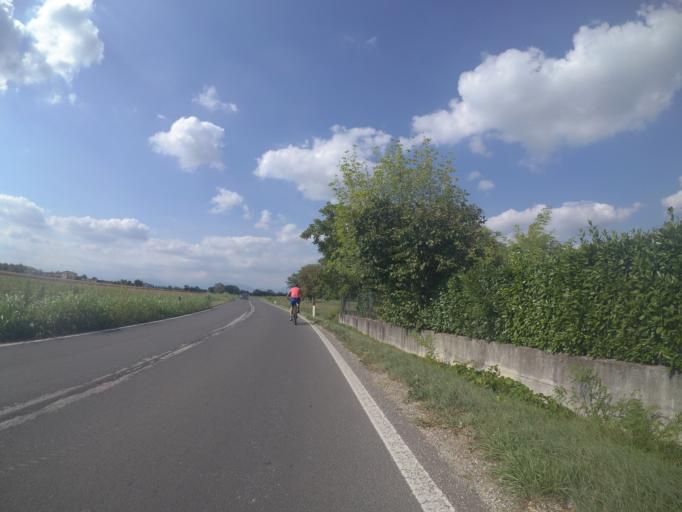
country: IT
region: Friuli Venezia Giulia
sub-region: Provincia di Udine
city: San Vito di Fagagna
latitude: 46.0704
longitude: 13.0837
